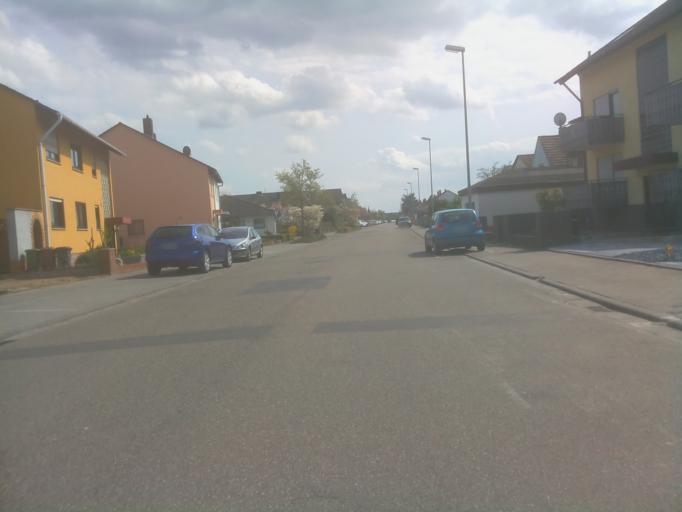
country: DE
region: Hesse
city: Lampertheim
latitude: 49.5851
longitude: 8.4871
